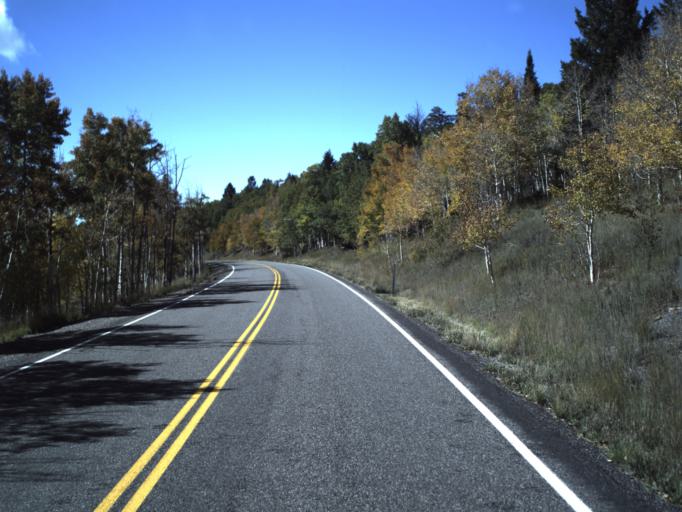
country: US
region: Utah
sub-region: Wayne County
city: Loa
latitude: 38.5394
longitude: -111.7357
